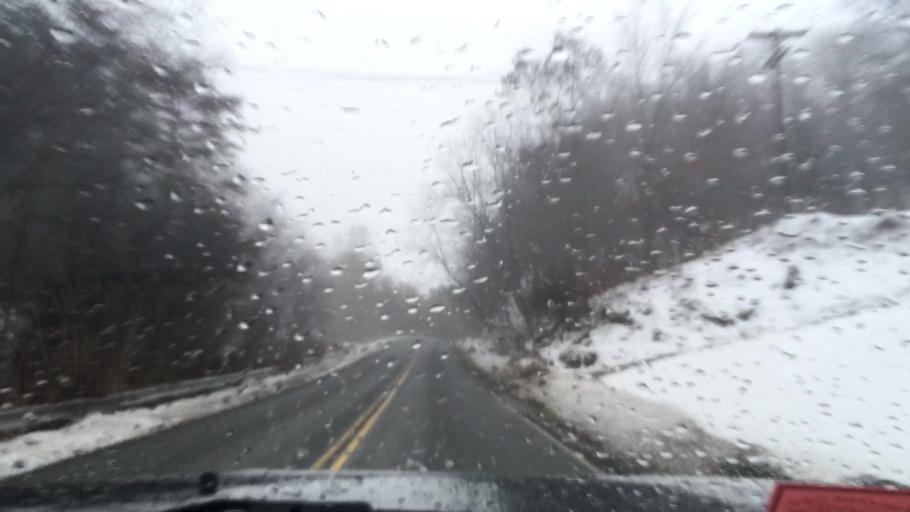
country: US
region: Virginia
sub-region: Pulaski County
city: Pulaski
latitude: 37.0283
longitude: -80.7190
